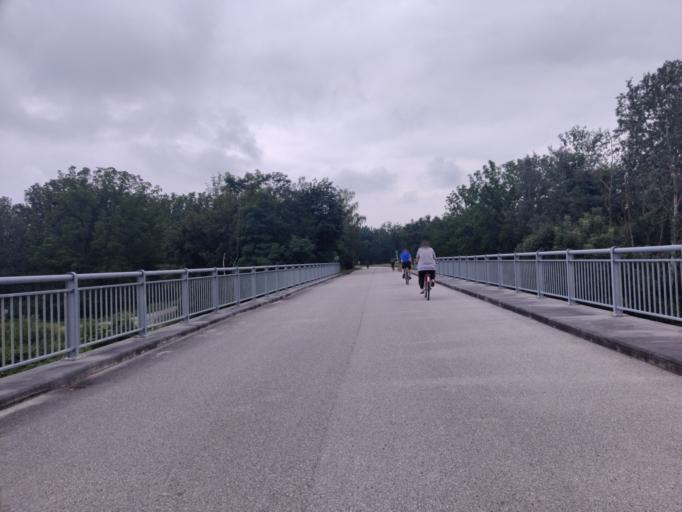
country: AT
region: Lower Austria
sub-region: Politischer Bezirk Tulln
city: Kirchberg am Wagram
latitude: 48.3695
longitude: 15.8549
